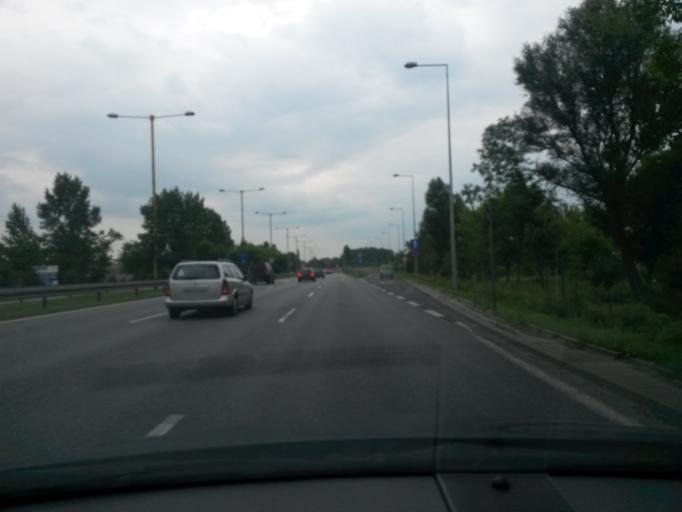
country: PL
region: Silesian Voivodeship
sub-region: Czestochowa
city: Czestochowa
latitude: 50.8092
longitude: 19.1359
